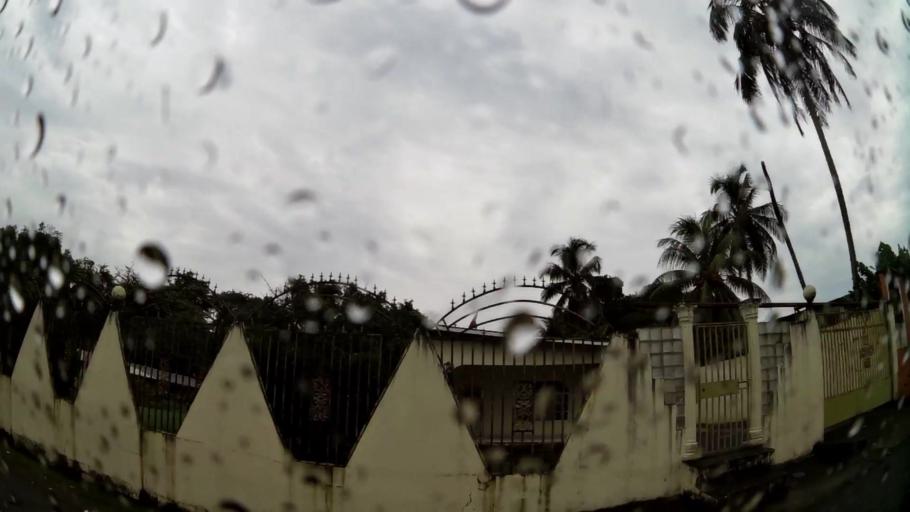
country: PA
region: Colon
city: Arco Iris
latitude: 9.3380
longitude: -79.8707
